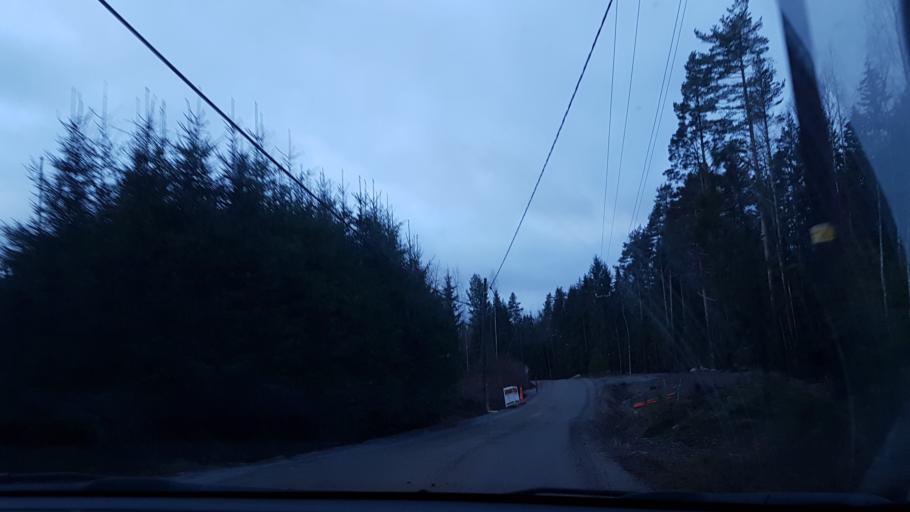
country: FI
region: Uusimaa
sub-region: Helsinki
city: Sibbo
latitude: 60.2858
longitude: 25.1741
